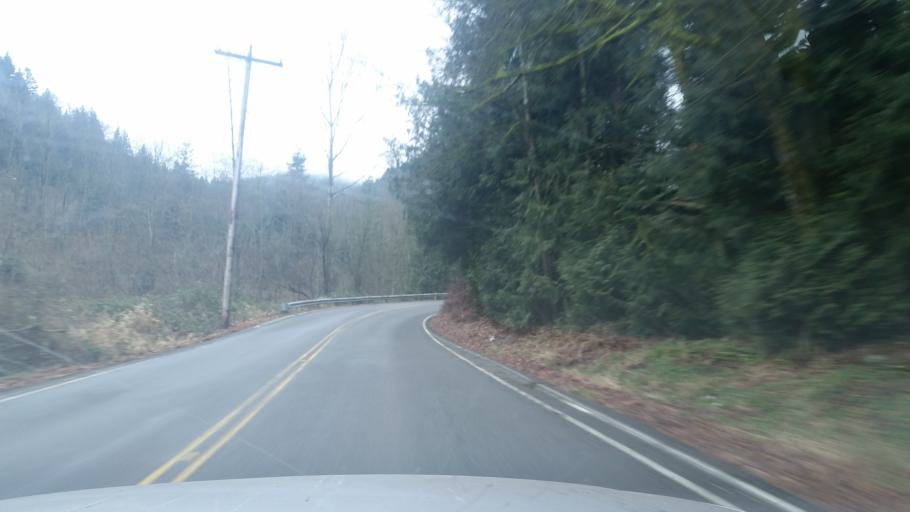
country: US
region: Washington
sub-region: King County
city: Issaquah
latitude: 47.5363
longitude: -121.9746
